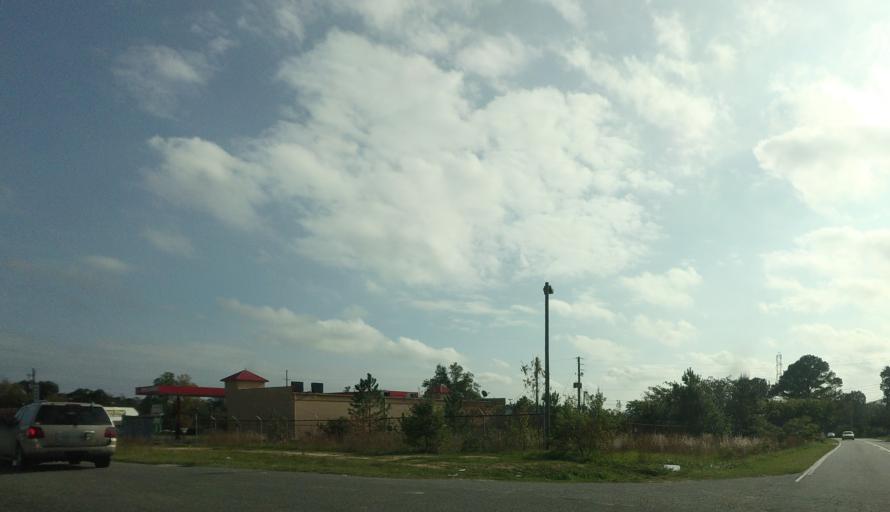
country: US
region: Georgia
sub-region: Bibb County
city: Macon
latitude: 32.7990
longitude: -83.6667
